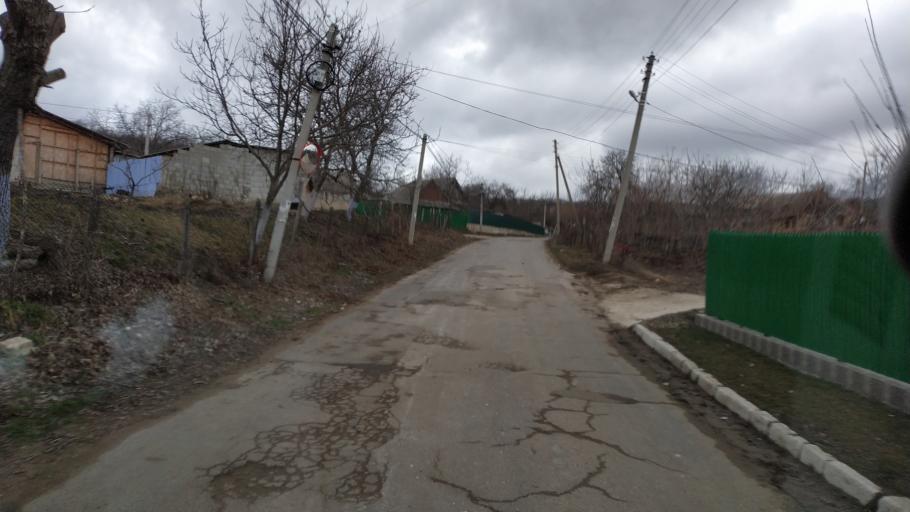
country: MD
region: Calarasi
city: Calarasi
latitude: 47.2137
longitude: 28.2598
